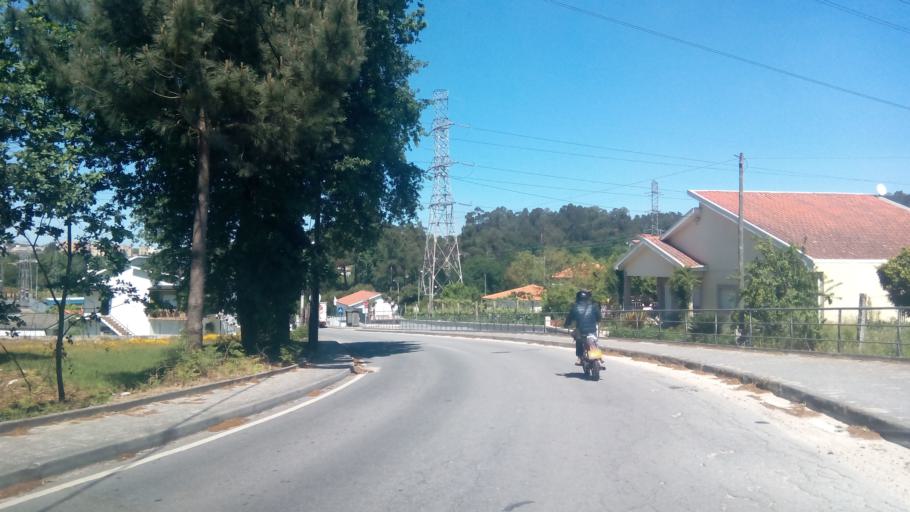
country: PT
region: Porto
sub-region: Paredes
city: Casteloes de Cepeda
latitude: 41.1880
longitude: -8.3386
